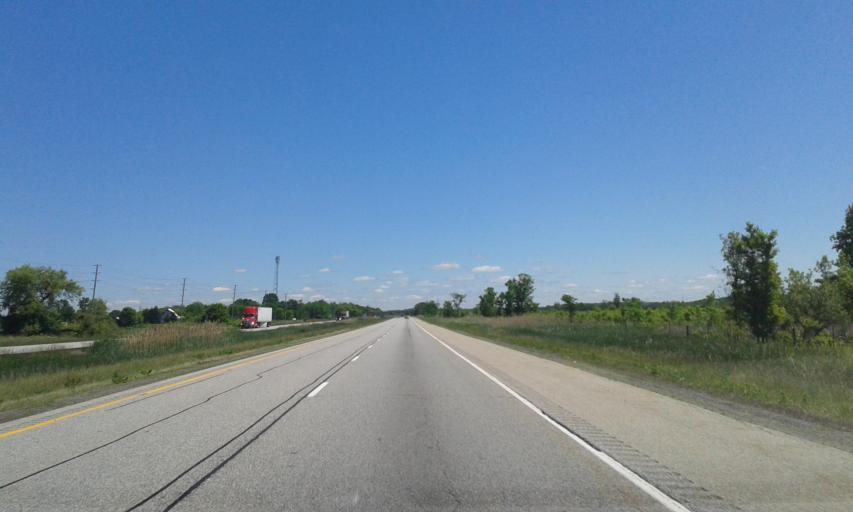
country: US
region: New York
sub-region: St. Lawrence County
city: Ogdensburg
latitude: 44.8881
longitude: -75.2696
